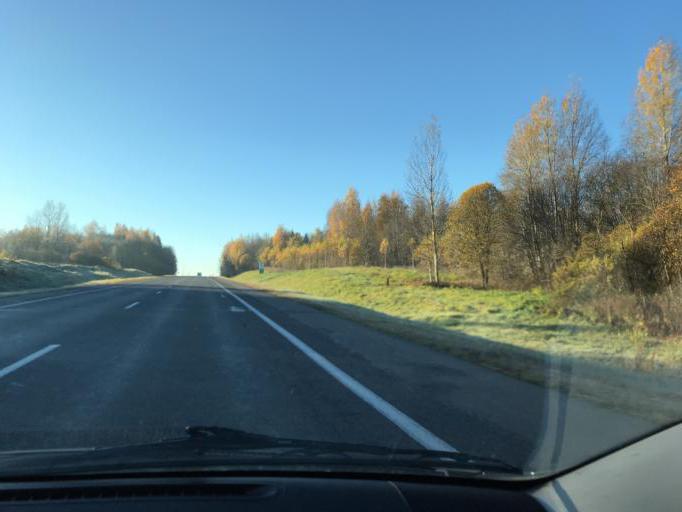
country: BY
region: Vitebsk
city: Vitebsk
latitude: 54.9164
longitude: 30.3752
